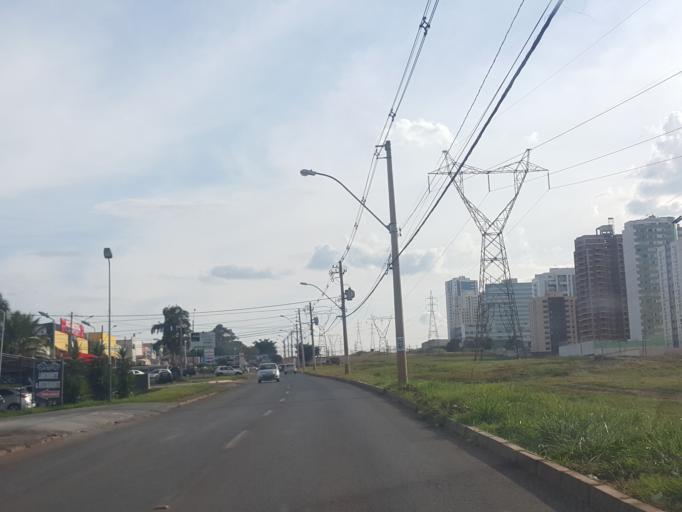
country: BR
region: Federal District
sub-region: Brasilia
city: Brasilia
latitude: -15.8454
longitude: -48.0230
